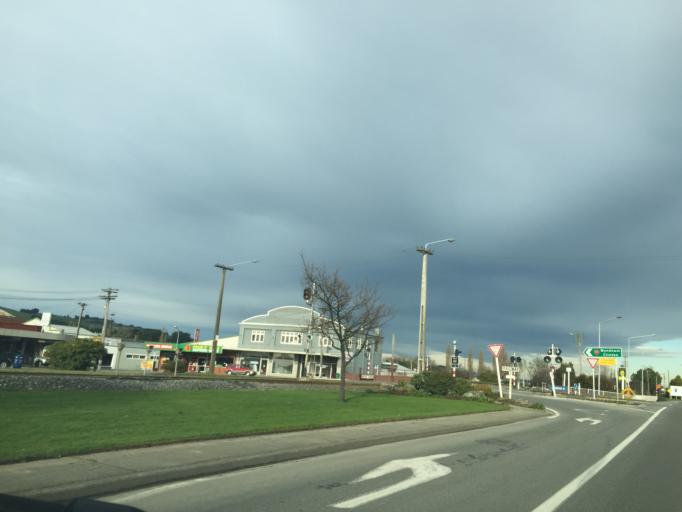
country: NZ
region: Southland
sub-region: Gore District
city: Gore
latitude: -46.1935
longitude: 168.8659
